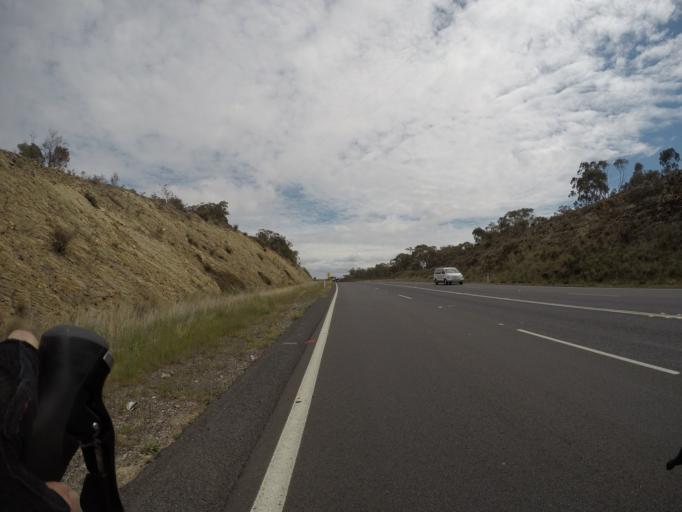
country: AU
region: New South Wales
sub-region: Bathurst Regional
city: Kelso
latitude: -33.4366
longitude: 149.7523
